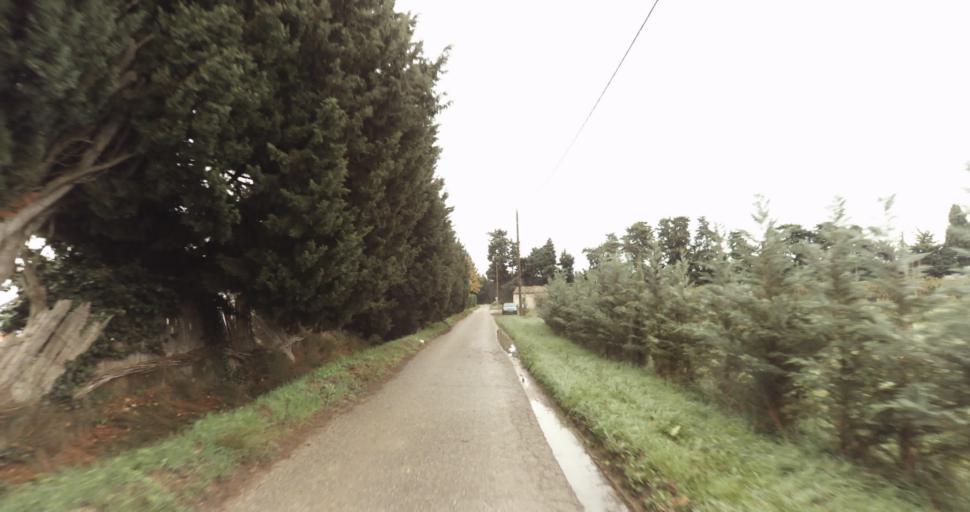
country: FR
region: Provence-Alpes-Cote d'Azur
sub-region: Departement des Bouches-du-Rhone
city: Rognonas
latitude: 43.9089
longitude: 4.7980
